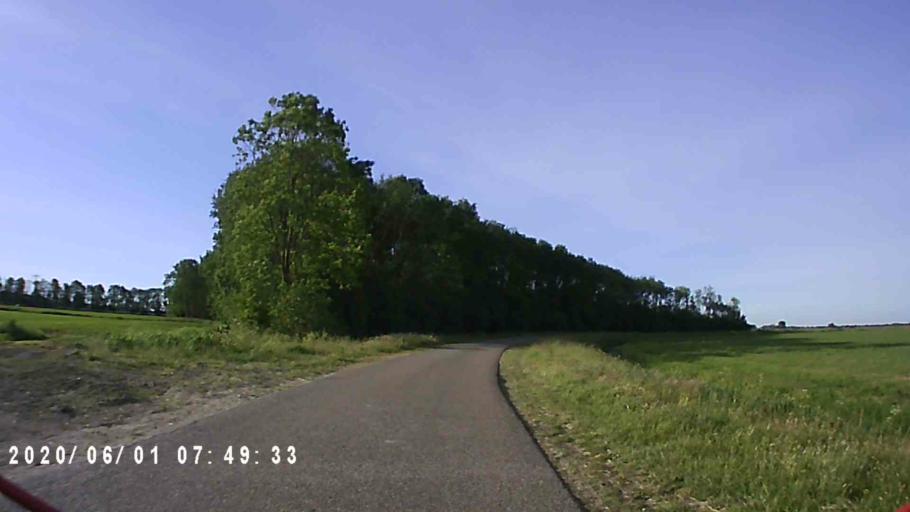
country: NL
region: Friesland
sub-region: Gemeente Dantumadiel
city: Rinsumageast
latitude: 53.2918
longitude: 5.9544
